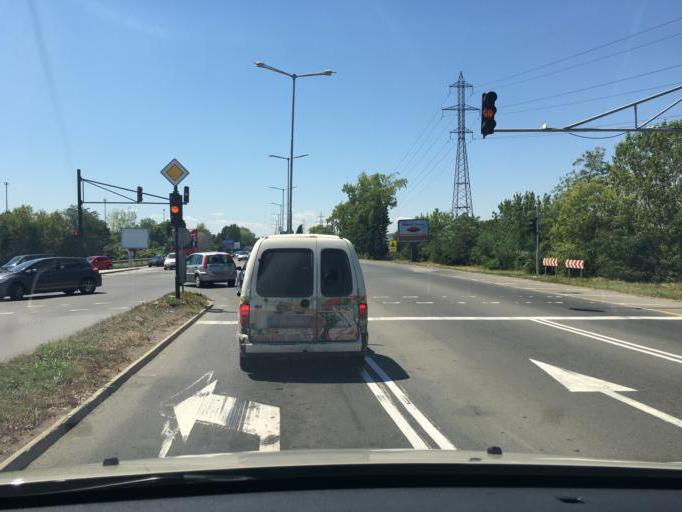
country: BG
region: Burgas
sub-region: Obshtina Burgas
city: Burgas
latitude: 42.4937
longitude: 27.4506
